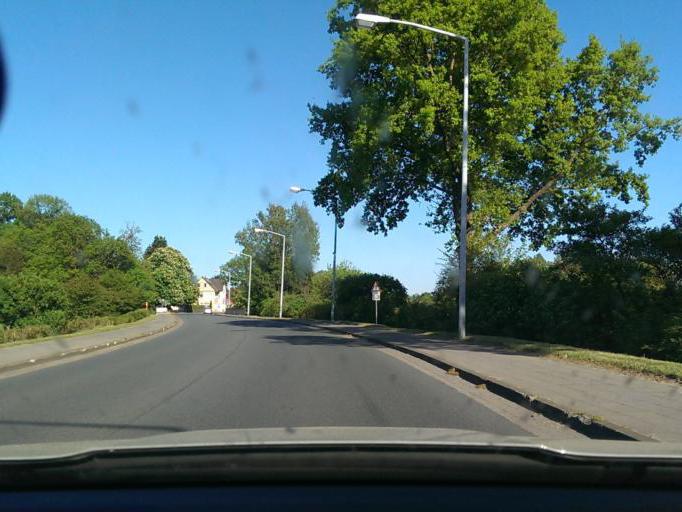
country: DE
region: Lower Saxony
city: Wietze
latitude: 52.6483
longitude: 9.8522
